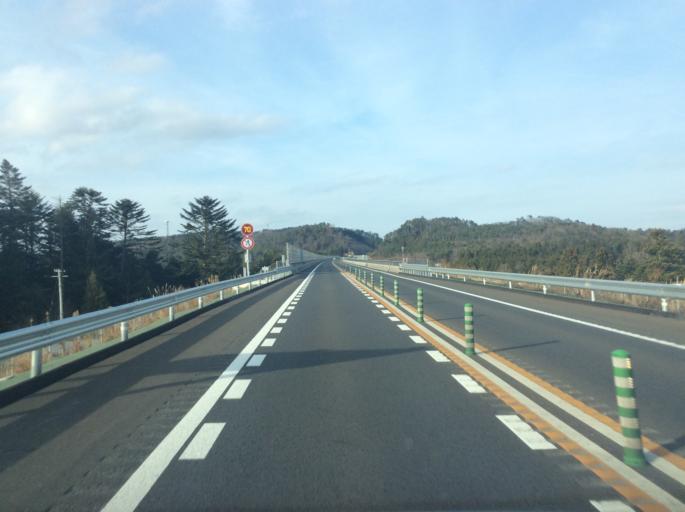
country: JP
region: Fukushima
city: Namie
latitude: 37.4297
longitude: 140.9605
